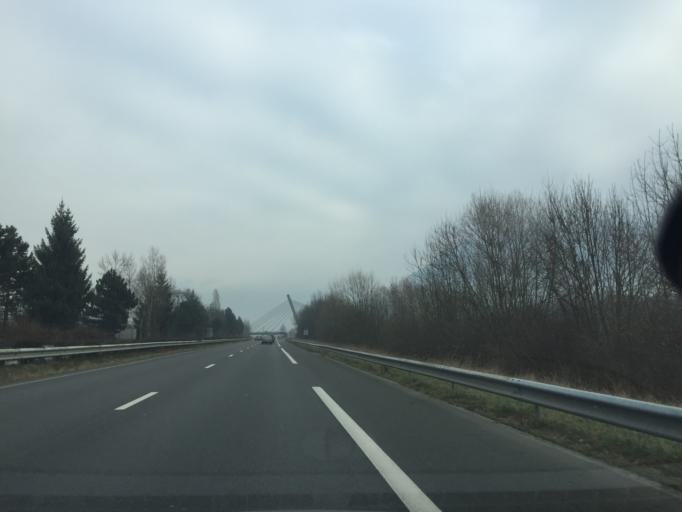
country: FR
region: Rhone-Alpes
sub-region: Departement de la Savoie
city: Gilly-sur-Isere
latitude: 45.6511
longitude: 6.3496
